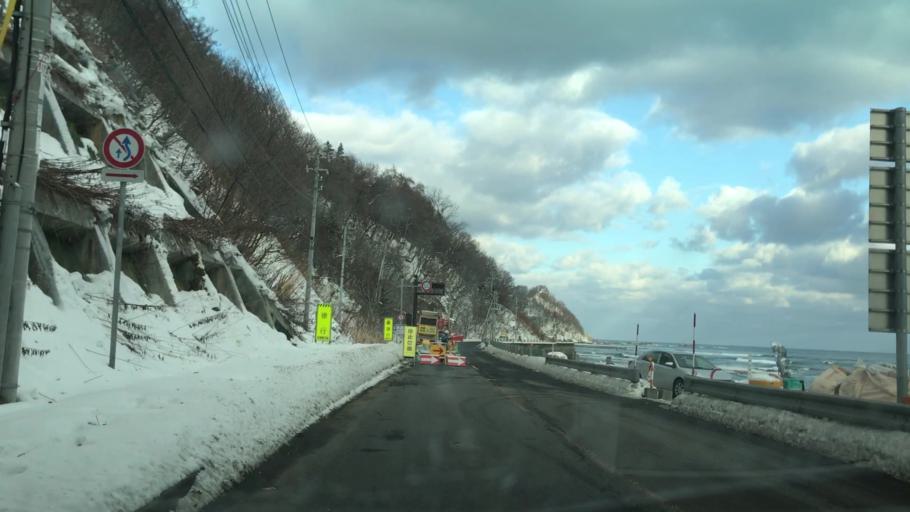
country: JP
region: Hokkaido
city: Yoichi
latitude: 43.2855
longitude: 140.6347
